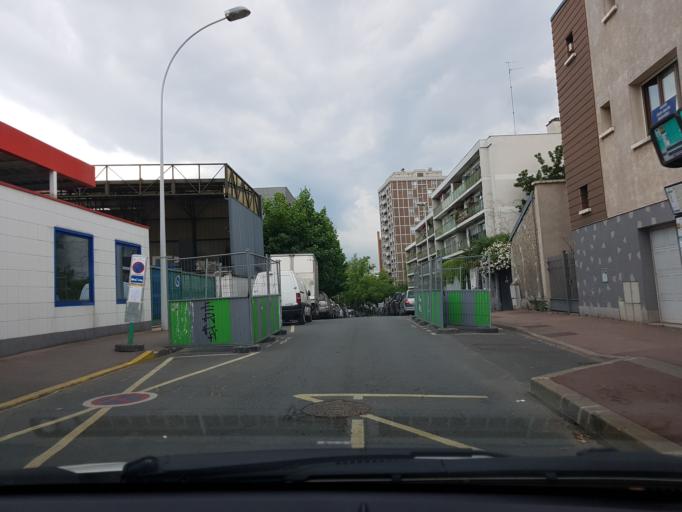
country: FR
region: Ile-de-France
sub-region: Departement du Val-de-Marne
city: Gentilly
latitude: 48.8135
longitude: 2.3503
